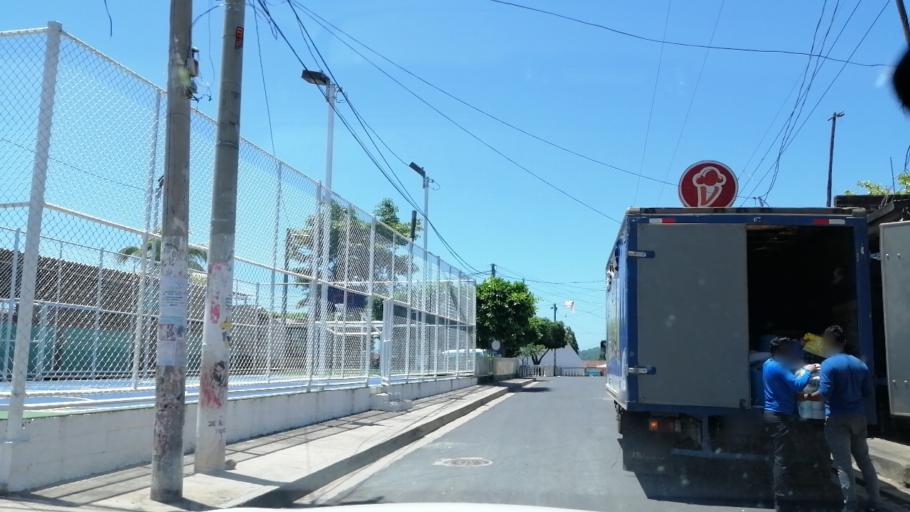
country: SV
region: San Miguel
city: Ciudad Barrios
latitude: 13.8305
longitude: -88.2281
